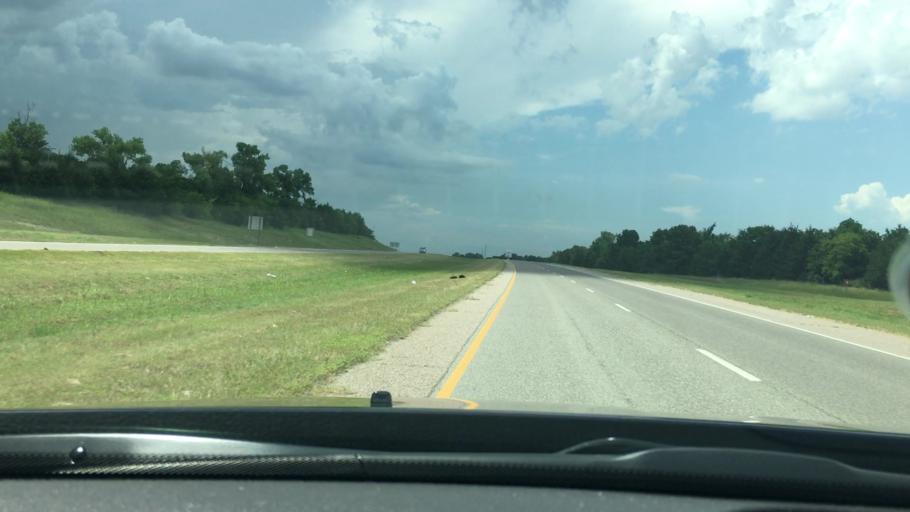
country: US
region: Oklahoma
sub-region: Pontotoc County
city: Ada
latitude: 34.7391
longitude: -96.6453
